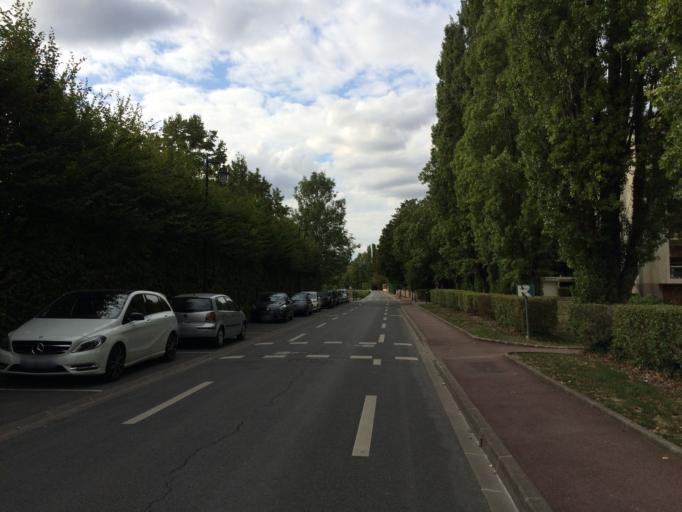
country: FR
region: Ile-de-France
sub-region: Departement de l'Essonne
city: Soisy-sur-Seine
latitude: 48.6497
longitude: 2.4416
